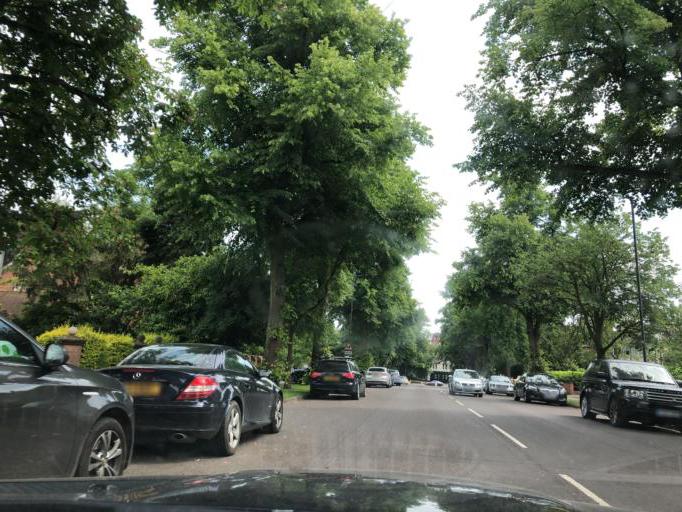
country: GB
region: England
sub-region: Warwickshire
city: Royal Leamington Spa
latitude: 52.2973
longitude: -1.5416
